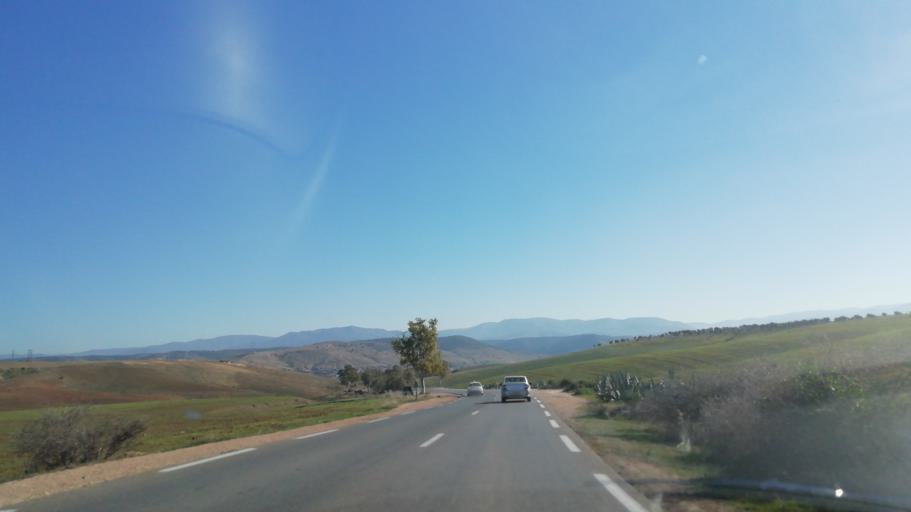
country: DZ
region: Tlemcen
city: Nedroma
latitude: 34.8312
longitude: -1.6690
